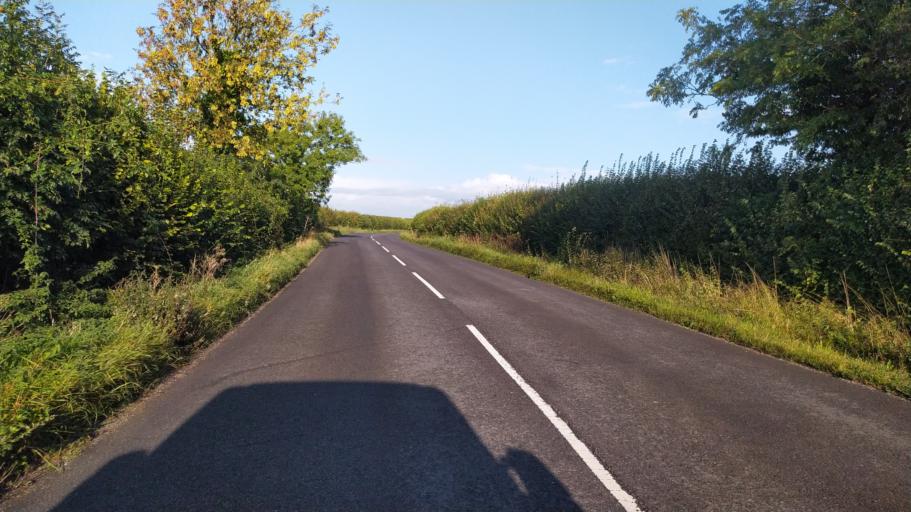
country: GB
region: England
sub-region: Dorset
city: Three Legged Cross
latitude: 50.8692
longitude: -1.9626
